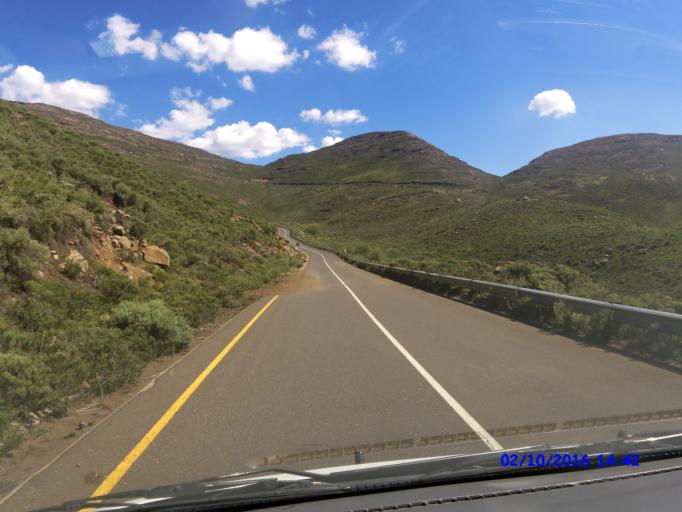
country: LS
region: Maseru
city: Nako
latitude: -29.5305
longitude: 28.0588
